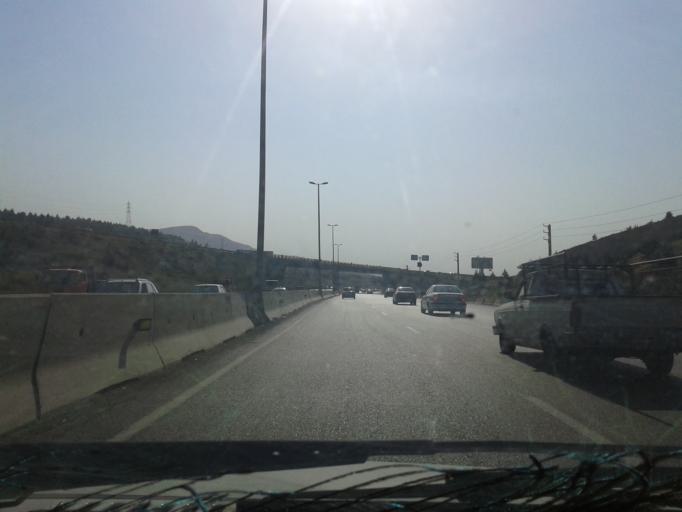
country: IR
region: Tehran
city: Tehran
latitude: 35.7322
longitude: 51.6484
